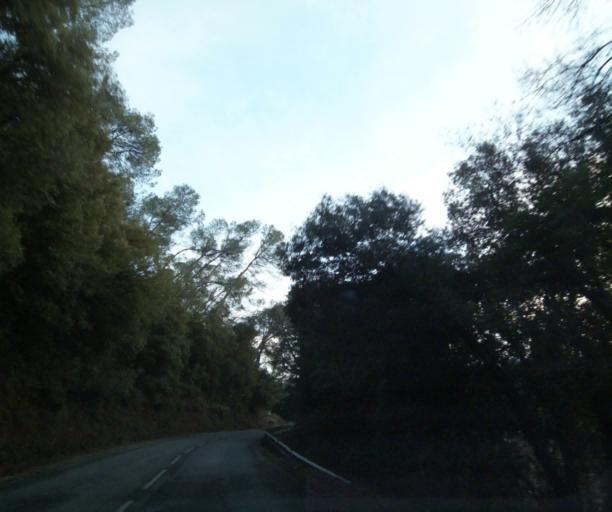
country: FR
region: Provence-Alpes-Cote d'Azur
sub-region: Departement du Var
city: Trans-en-Provence
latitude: 43.4979
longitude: 6.4990
